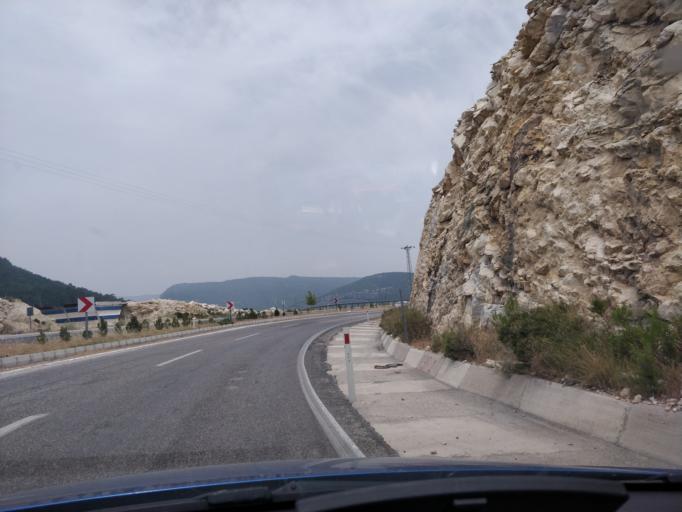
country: TR
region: Mersin
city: Tasucu
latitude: 36.3989
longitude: 33.8463
